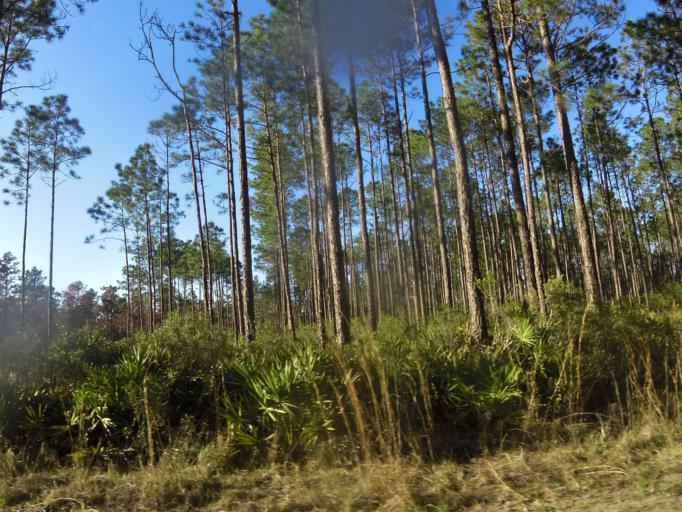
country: US
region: Florida
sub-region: Clay County
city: Middleburg
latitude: 30.1481
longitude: -81.9002
